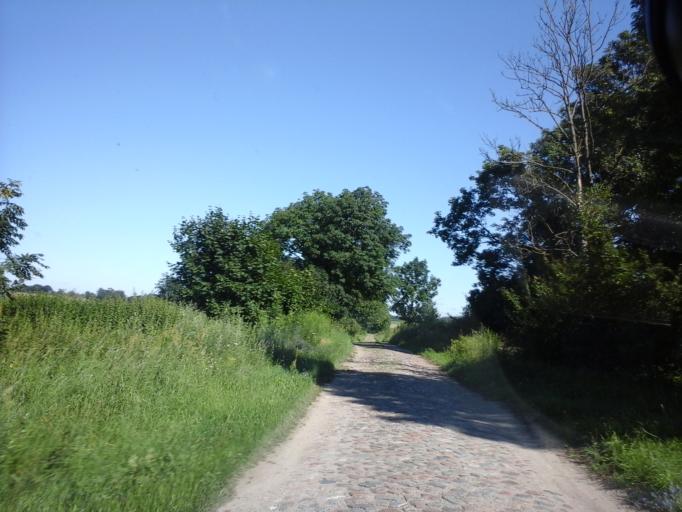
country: PL
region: West Pomeranian Voivodeship
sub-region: Powiat choszczenski
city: Choszczno
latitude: 53.1922
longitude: 15.4734
